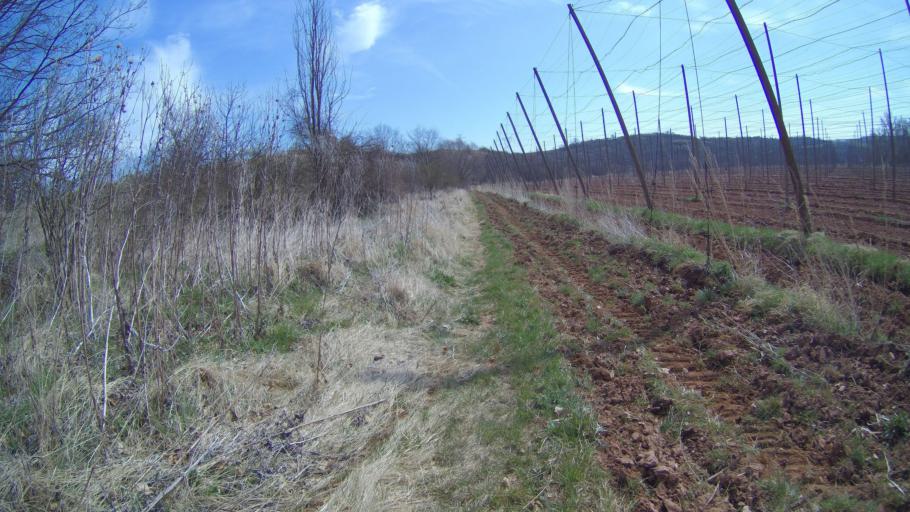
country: CZ
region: Ustecky
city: Mecholupy
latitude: 50.2284
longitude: 13.4818
